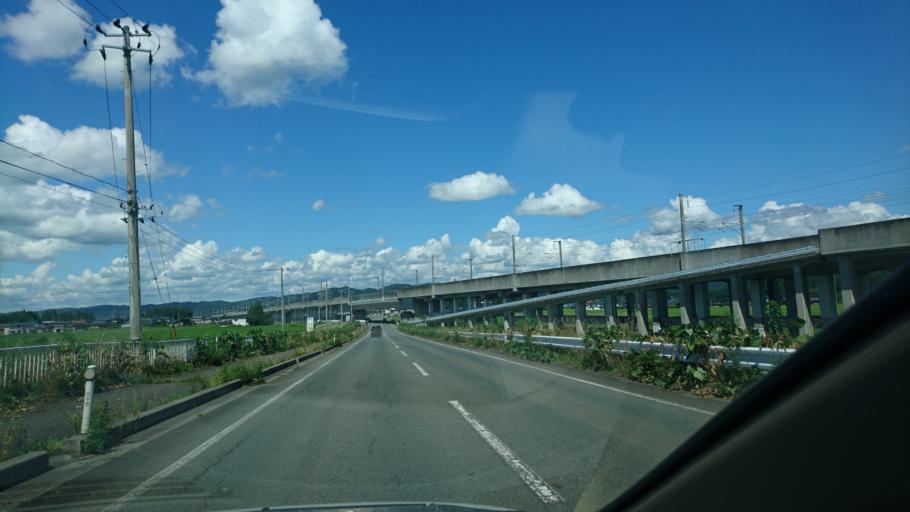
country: JP
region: Iwate
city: Kitakami
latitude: 39.3015
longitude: 141.1341
